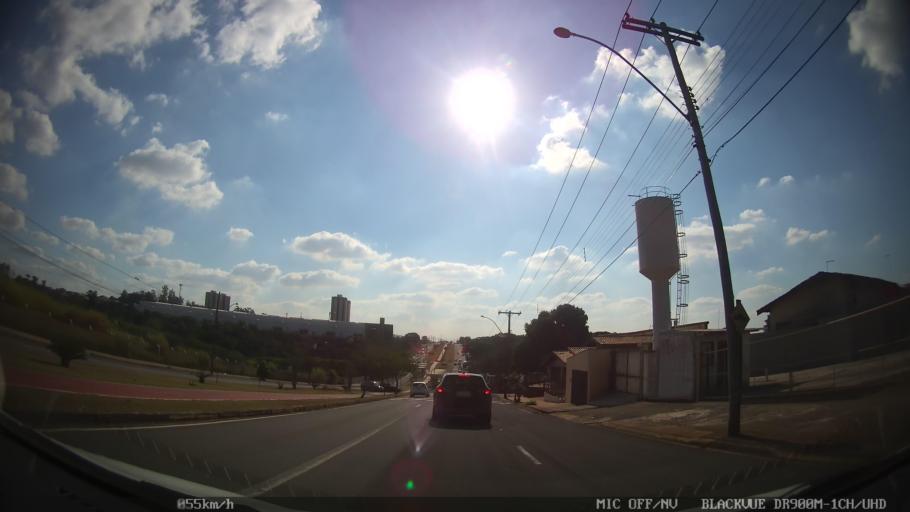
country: BR
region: Sao Paulo
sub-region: Nova Odessa
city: Nova Odessa
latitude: -22.7810
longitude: -47.3043
